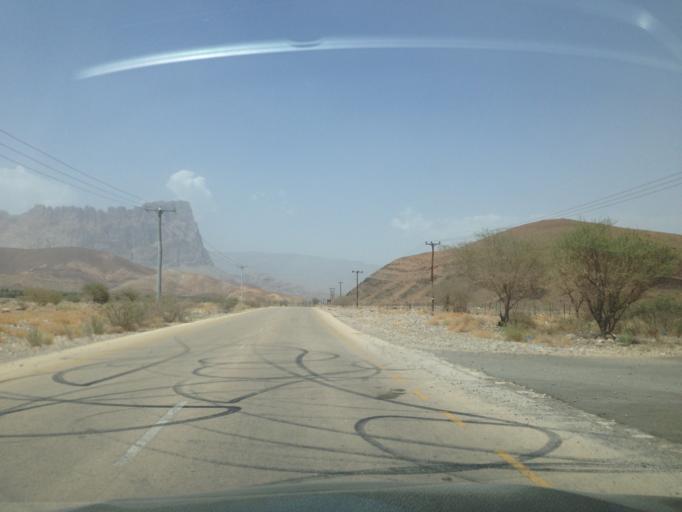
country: OM
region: Az Zahirah
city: `Ibri
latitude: 23.1982
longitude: 56.9372
